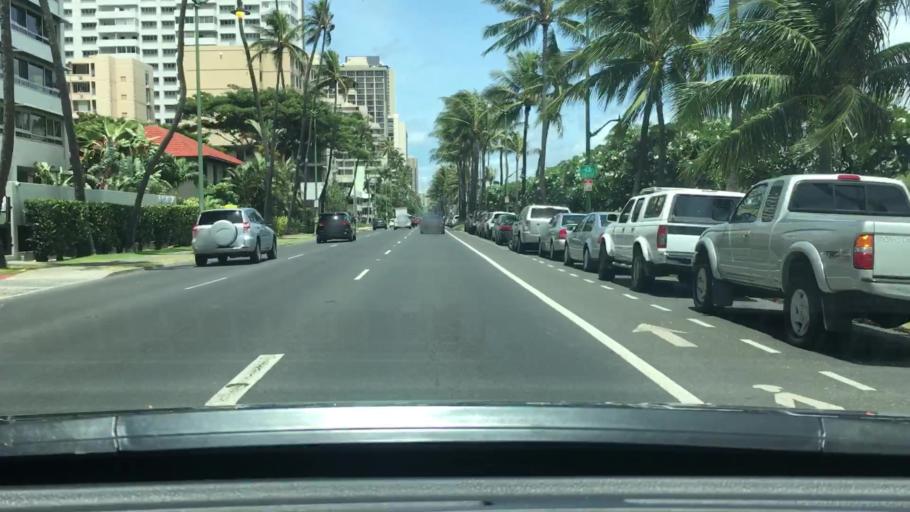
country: US
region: Hawaii
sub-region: Honolulu County
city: Honolulu
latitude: 21.2773
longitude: -157.8208
